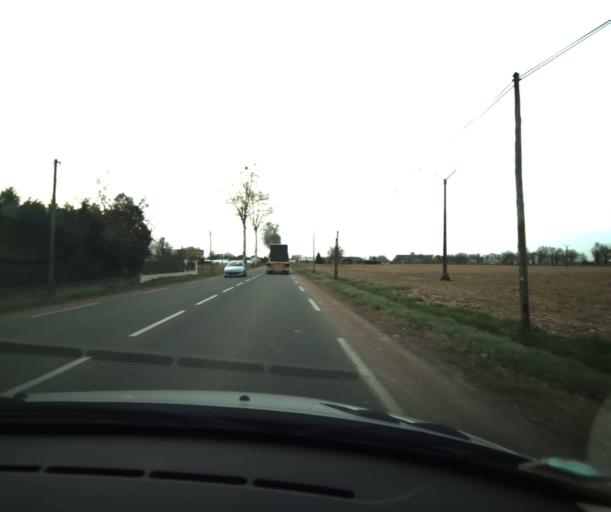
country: FR
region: Midi-Pyrenees
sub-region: Departement du Tarn-et-Garonne
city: Saint-Porquier
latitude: 44.0235
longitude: 1.1508
